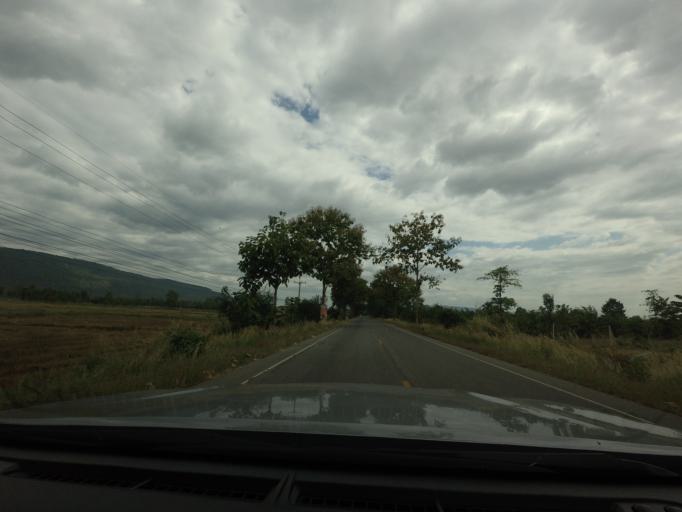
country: TH
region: Phitsanulok
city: Wang Thong
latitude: 16.7072
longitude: 100.4914
